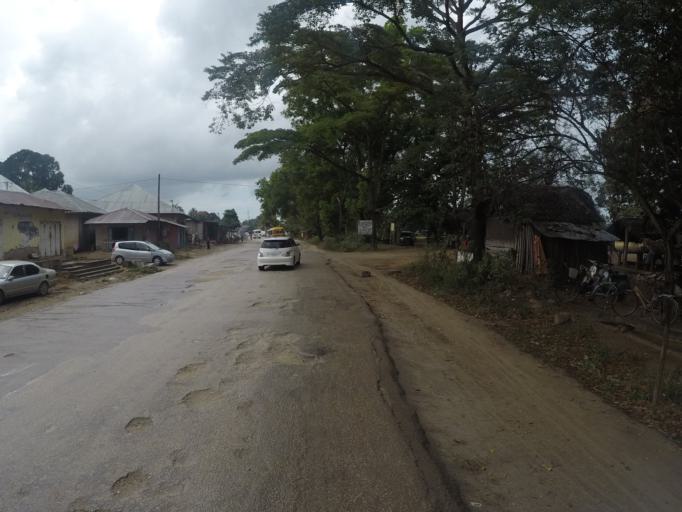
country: TZ
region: Zanzibar Urban/West
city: Zanzibar
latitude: -6.0930
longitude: 39.2192
